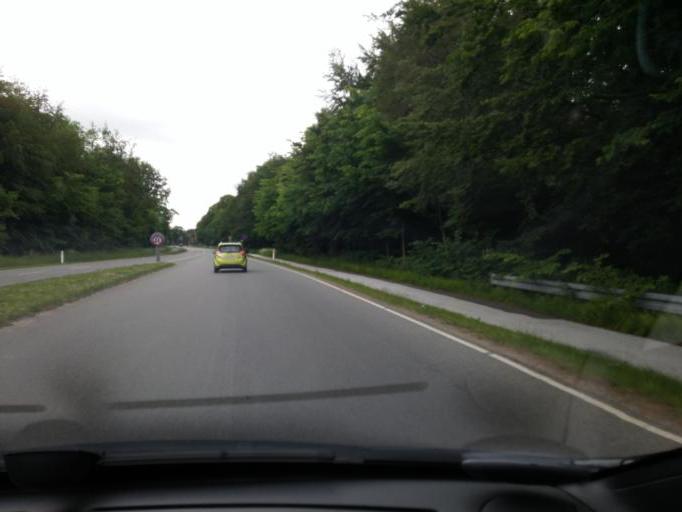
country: DK
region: Capital Region
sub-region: Hillerod Kommune
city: Hillerod
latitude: 55.9511
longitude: 12.3191
